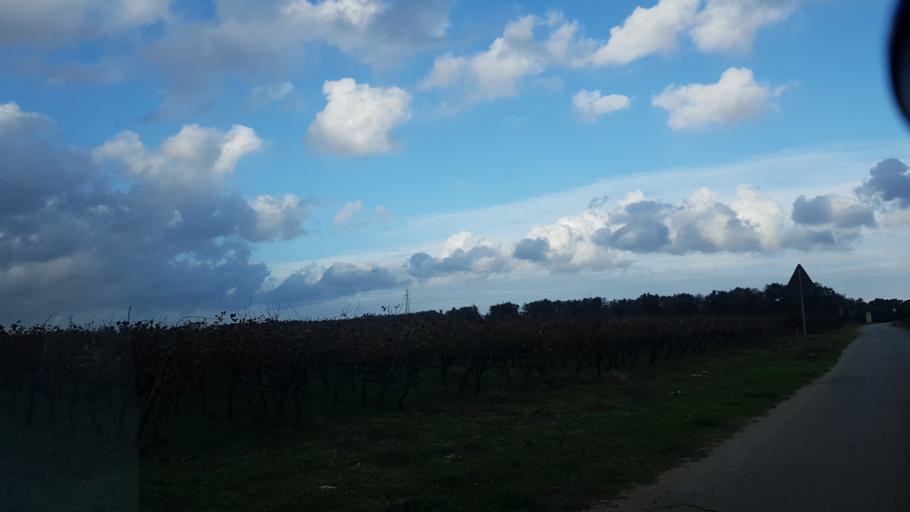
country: IT
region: Apulia
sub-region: Provincia di Brindisi
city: San Pietro Vernotico
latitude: 40.5080
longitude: 18.0194
